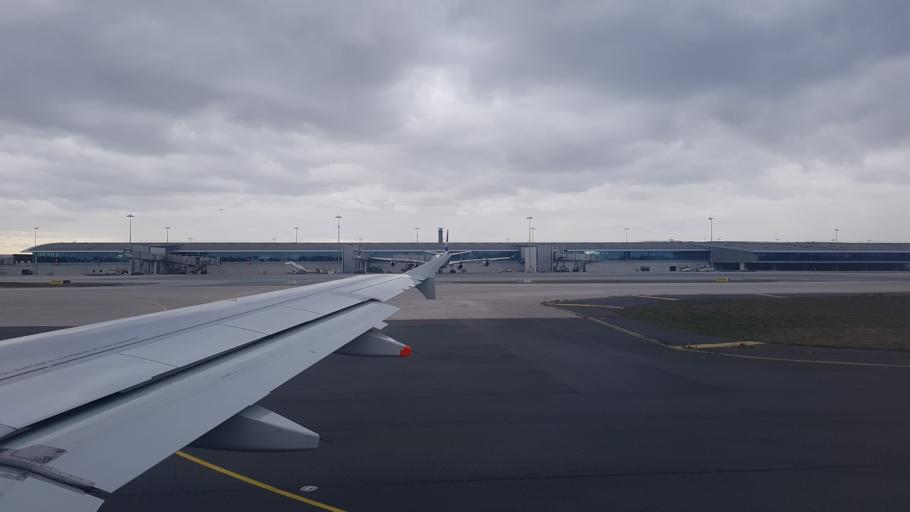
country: FR
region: Ile-de-France
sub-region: Departement de Seine-et-Marne
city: Mitry-Mory
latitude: 49.0031
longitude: 2.5960
